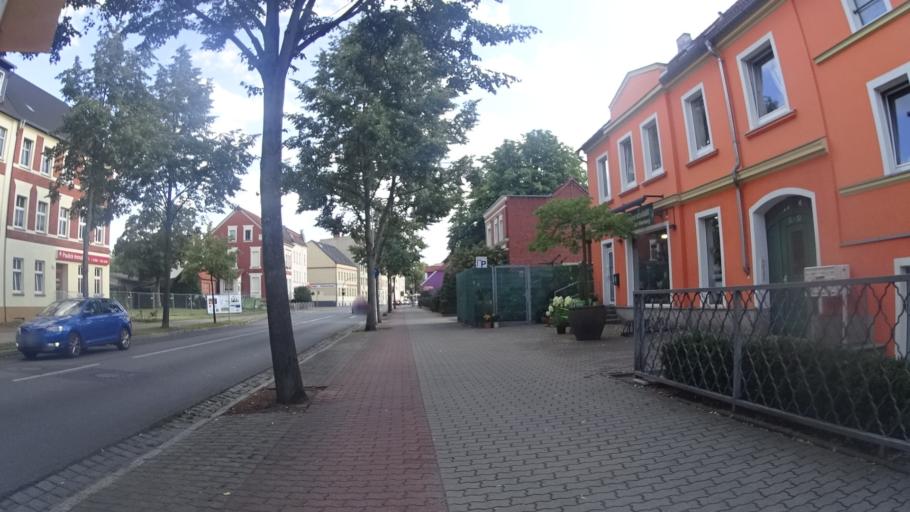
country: DE
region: Brandenburg
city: Rathenow
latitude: 52.6020
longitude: 12.3370
